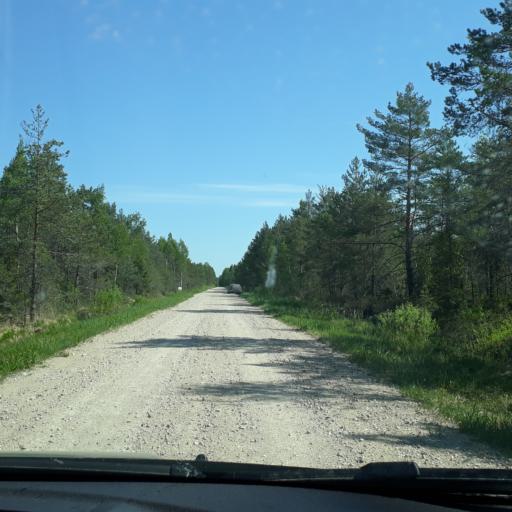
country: EE
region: Paernumaa
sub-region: Vaendra vald (alev)
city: Vandra
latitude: 58.7430
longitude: 24.9839
